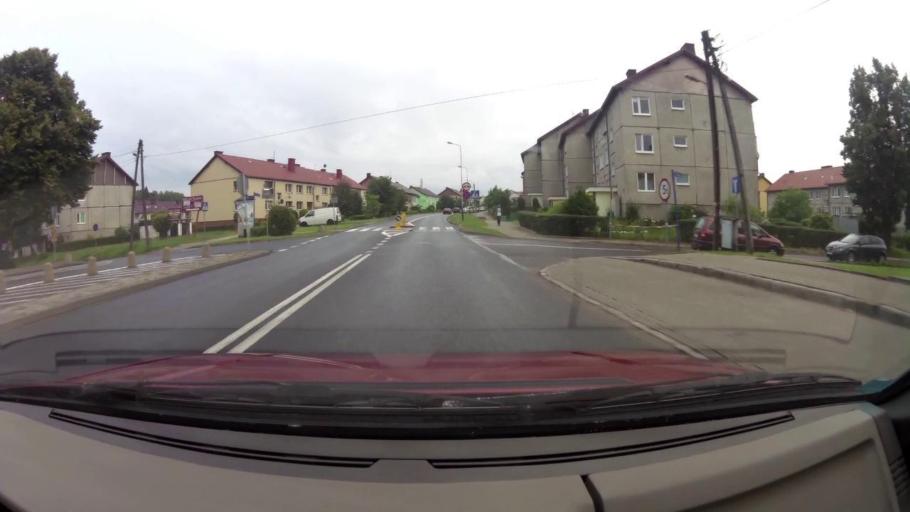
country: PL
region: West Pomeranian Voivodeship
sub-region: Powiat stargardzki
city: Chociwel
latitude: 53.4628
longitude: 15.3332
